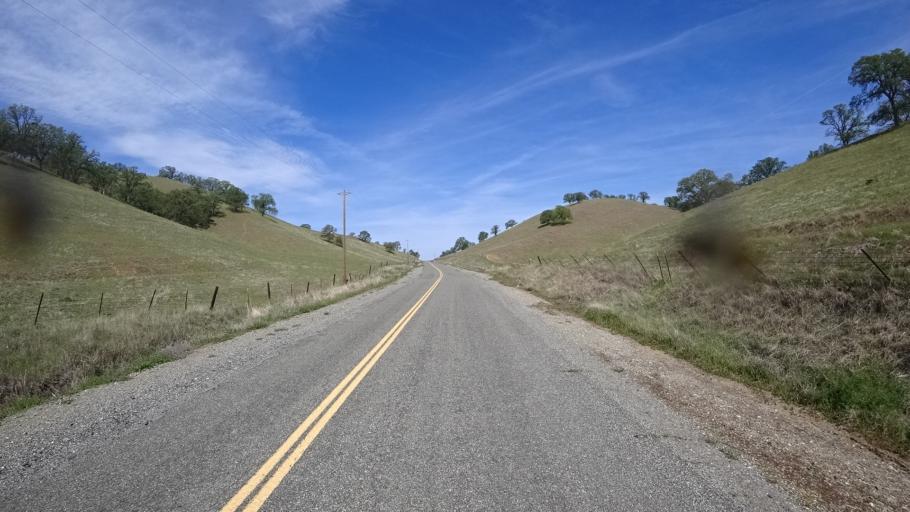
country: US
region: California
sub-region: Glenn County
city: Willows
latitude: 39.5694
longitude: -122.4429
